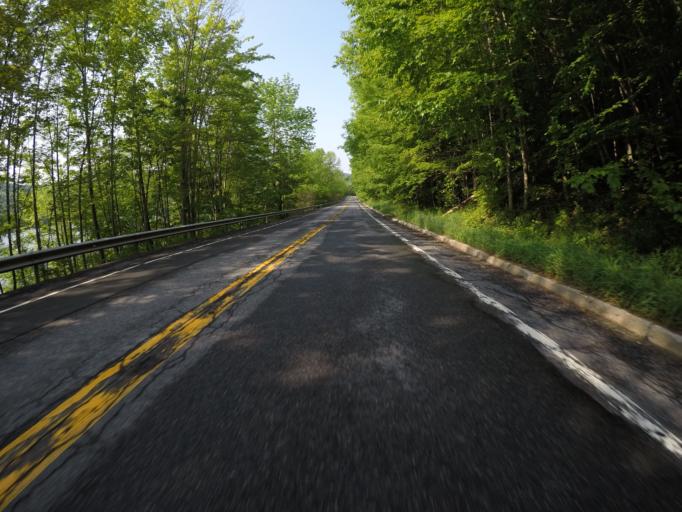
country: US
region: New York
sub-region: Sullivan County
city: Livingston Manor
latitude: 42.1082
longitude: -74.7801
